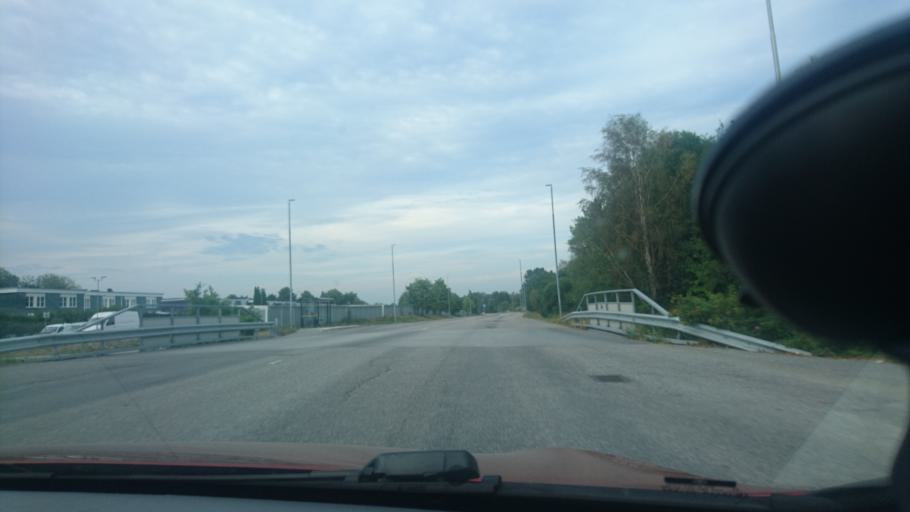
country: SE
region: Stockholm
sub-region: Upplands Vasby Kommun
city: Upplands Vaesby
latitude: 59.5057
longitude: 17.9159
